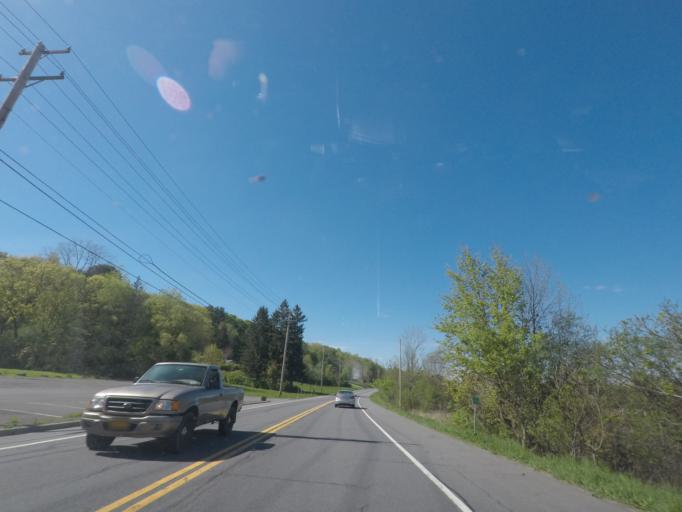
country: US
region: New York
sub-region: Albany County
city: Ravena
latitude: 42.4516
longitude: -73.8169
